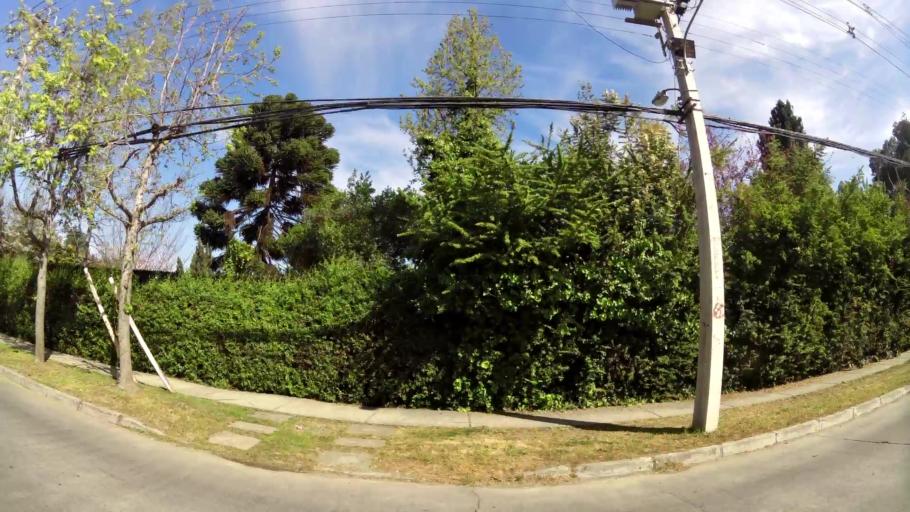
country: CL
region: Santiago Metropolitan
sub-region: Provincia de Santiago
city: Villa Presidente Frei, Nunoa, Santiago, Chile
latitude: -33.4357
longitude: -70.5328
